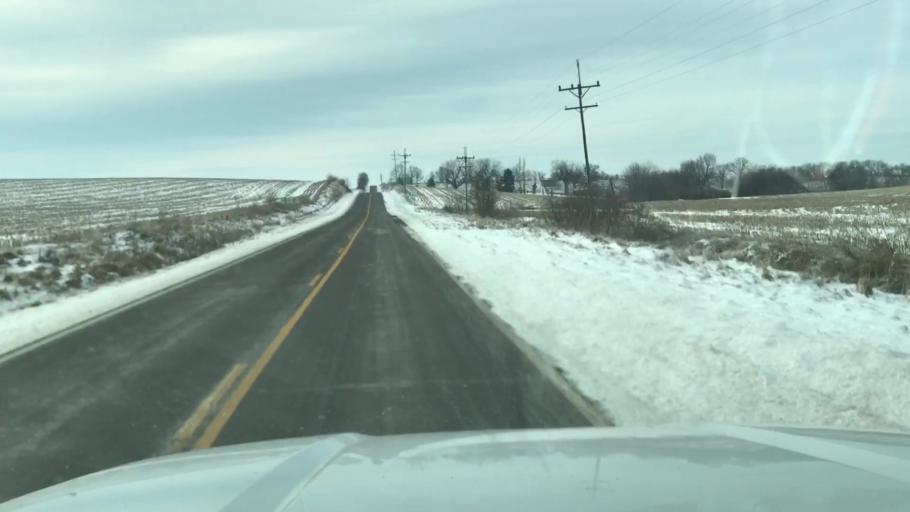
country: US
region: Missouri
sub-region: Holt County
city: Oregon
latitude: 40.0790
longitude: -95.1355
